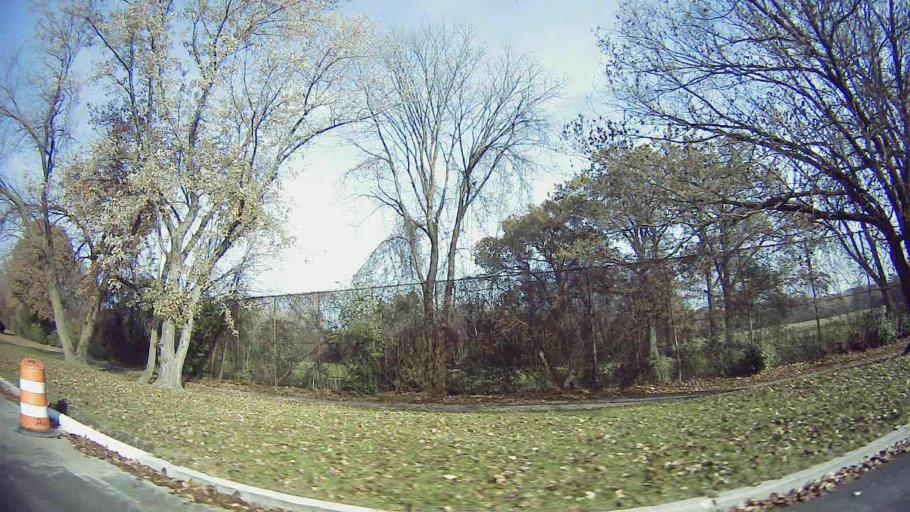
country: US
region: Michigan
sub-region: Wayne County
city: Highland Park
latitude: 42.4270
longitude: -83.1236
